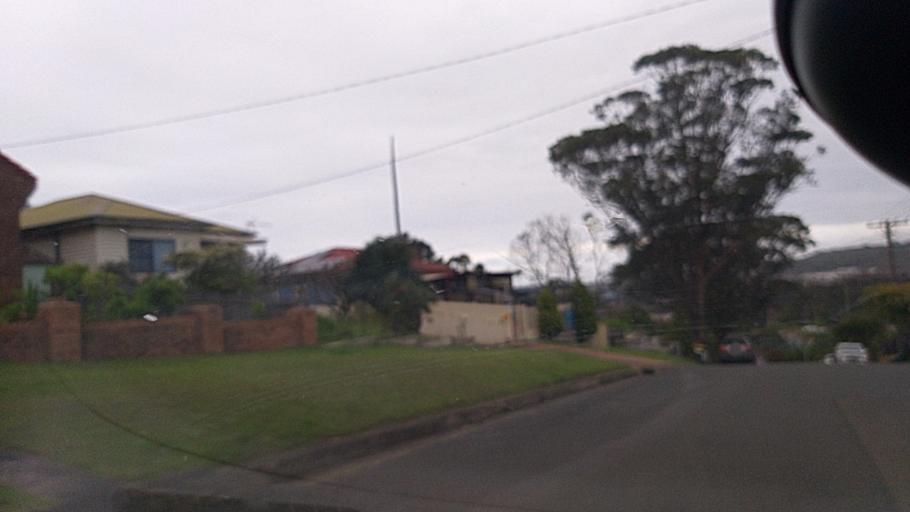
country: AU
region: New South Wales
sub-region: Wollongong
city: Mount Saint Thomas
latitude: -34.4415
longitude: 150.8710
